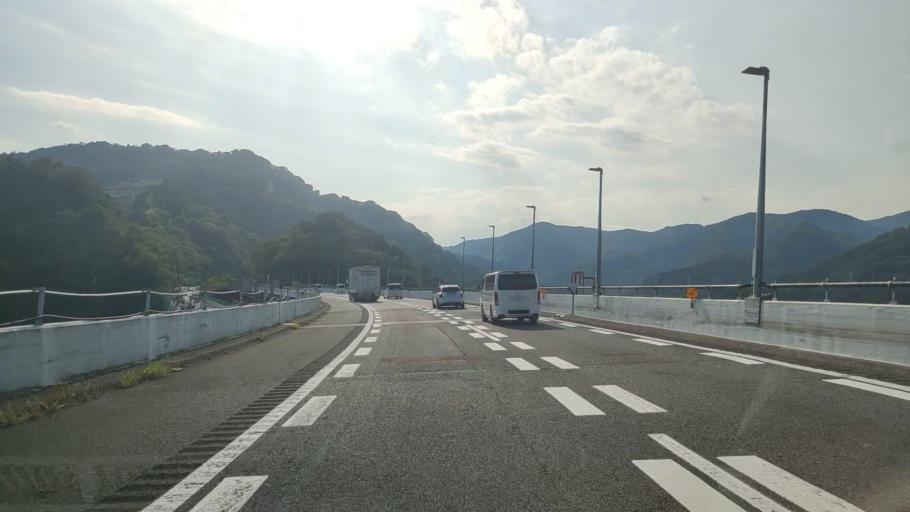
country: JP
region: Shizuoka
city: Gotemba
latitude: 35.3714
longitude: 139.0361
